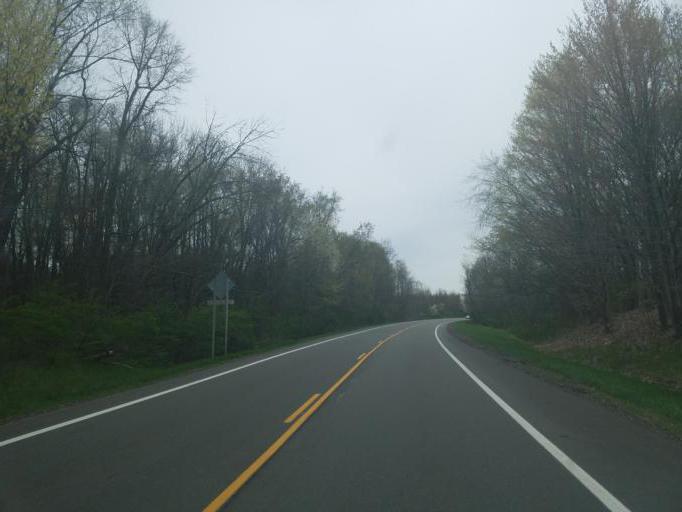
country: US
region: Ohio
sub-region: Wayne County
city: Doylestown
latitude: 40.9768
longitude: -81.7037
